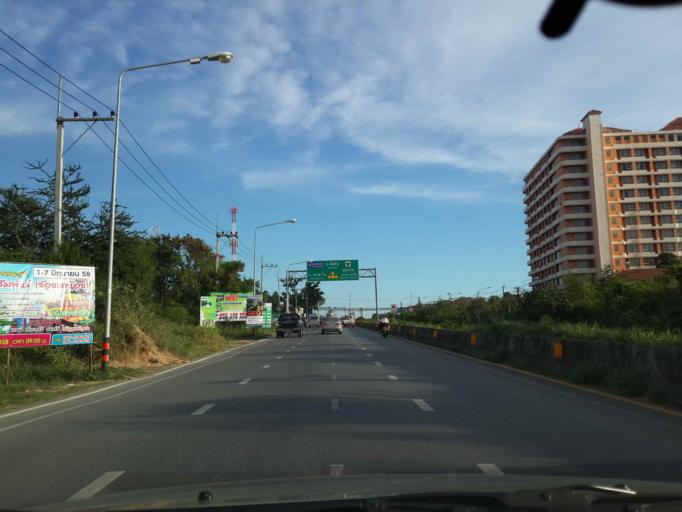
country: TH
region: Chon Buri
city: Phatthaya
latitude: 12.9114
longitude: 100.9018
